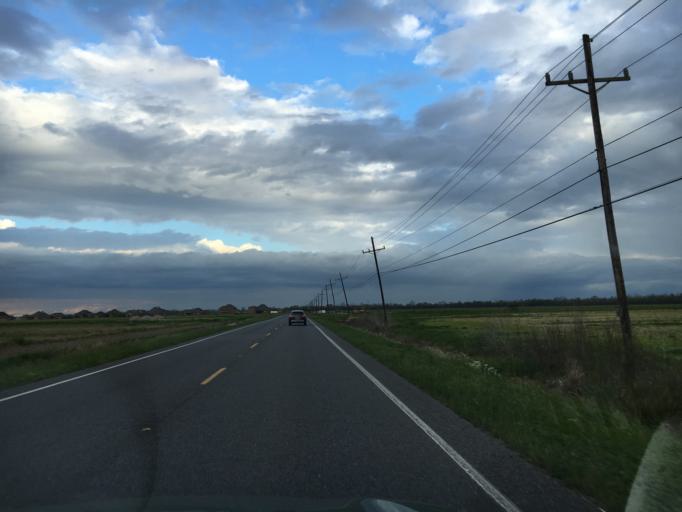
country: US
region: Louisiana
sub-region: West Baton Rouge Parish
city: Brusly
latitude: 30.4685
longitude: -91.3102
